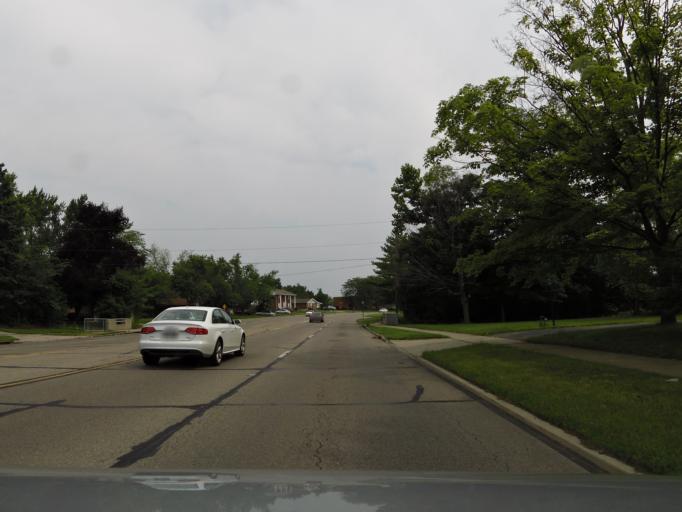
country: US
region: Ohio
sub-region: Montgomery County
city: Kettering
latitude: 39.6939
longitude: -84.1272
